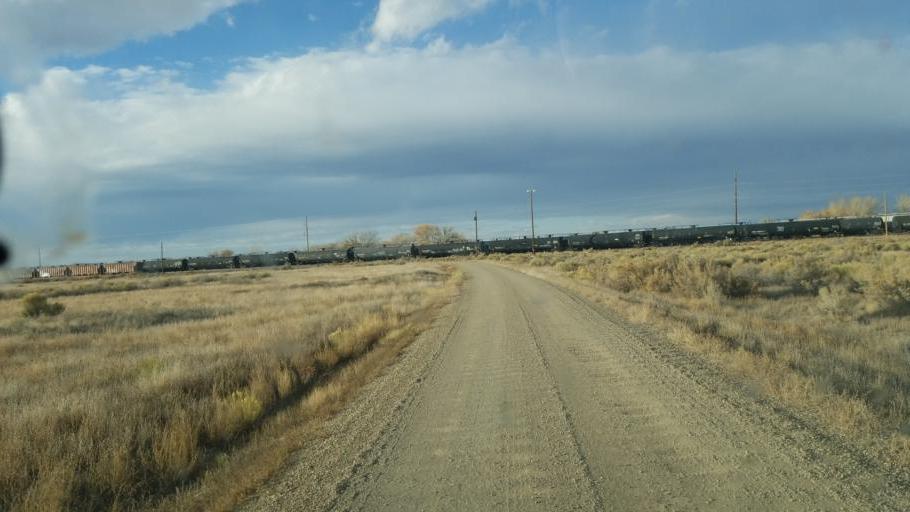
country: US
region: Colorado
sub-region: Alamosa County
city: Alamosa East
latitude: 37.4637
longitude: -105.8338
